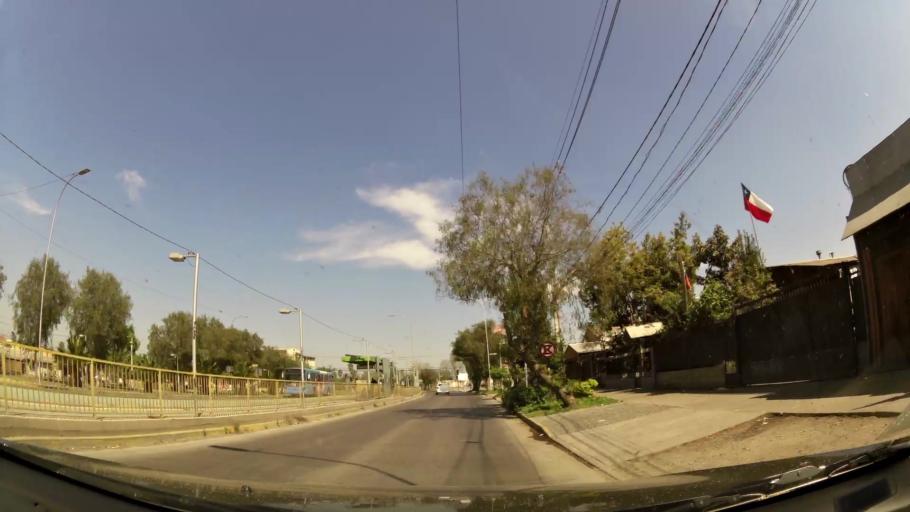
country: CL
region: Santiago Metropolitan
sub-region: Provincia de Santiago
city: Lo Prado
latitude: -33.4018
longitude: -70.7010
